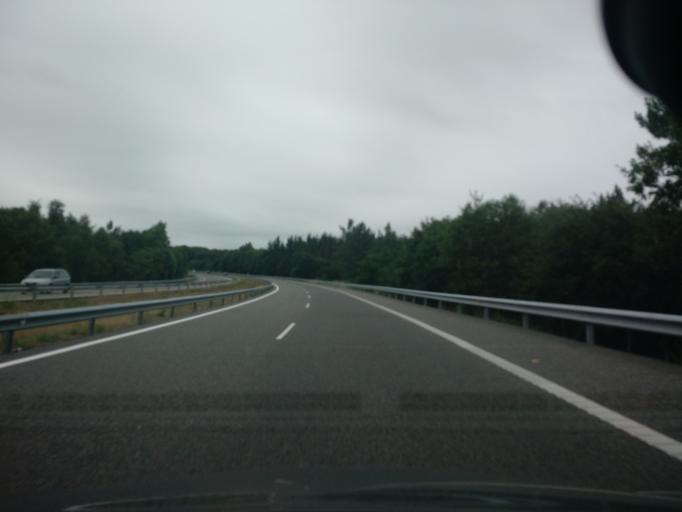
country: ES
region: Galicia
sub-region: Provincia da Coruna
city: Oroso
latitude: 42.9253
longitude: -8.4779
